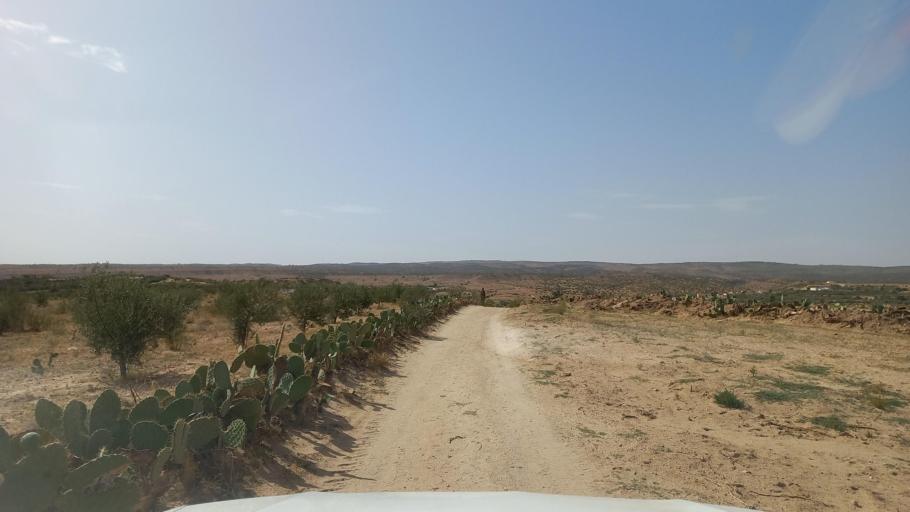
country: TN
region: Al Qasrayn
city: Kasserine
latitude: 35.2989
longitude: 8.9486
